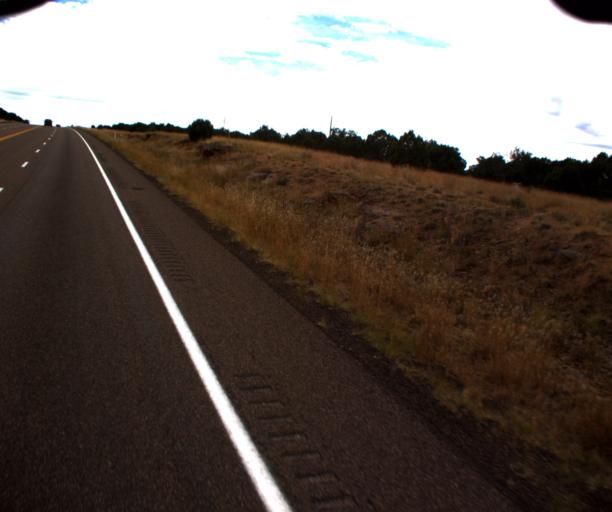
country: US
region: Arizona
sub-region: Navajo County
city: White Mountain Lake
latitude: 34.3421
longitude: -110.0514
